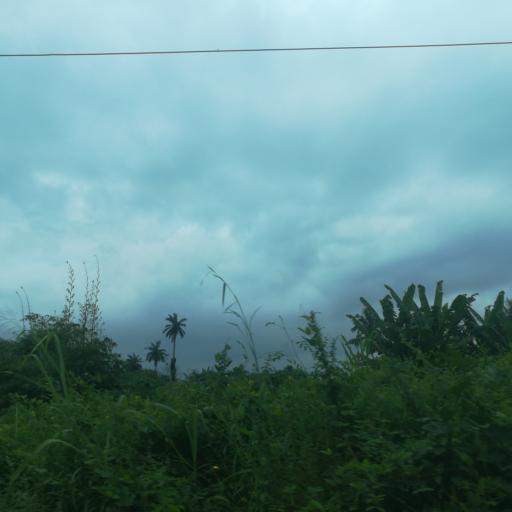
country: NG
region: Lagos
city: Ejirin
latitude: 6.6619
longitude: 3.8095
